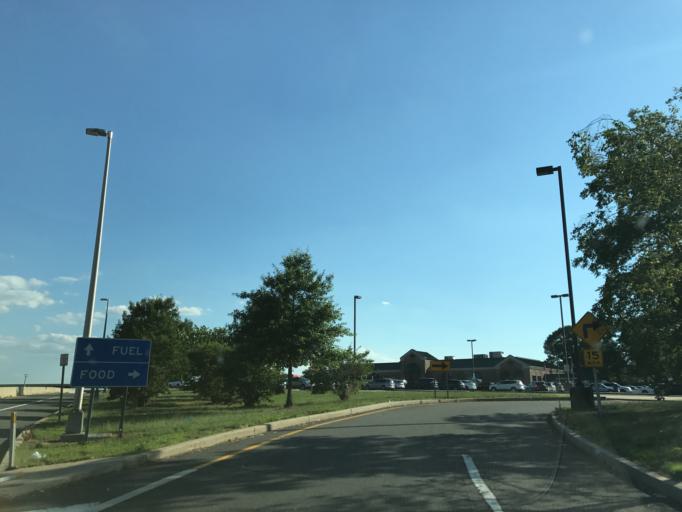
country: US
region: New Jersey
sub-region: Middlesex County
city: Rossmoor
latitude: 40.3222
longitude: -74.4866
